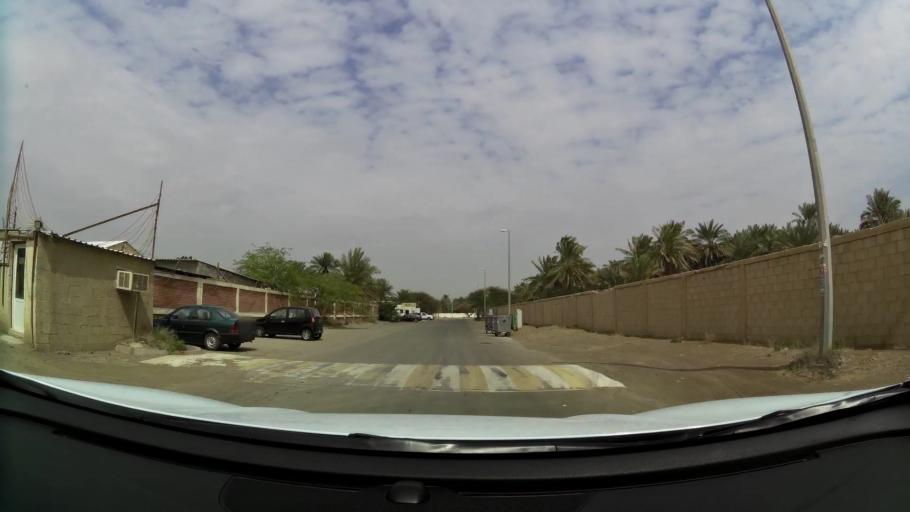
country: OM
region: Al Buraimi
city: Al Buraymi
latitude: 24.2159
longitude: 55.7957
